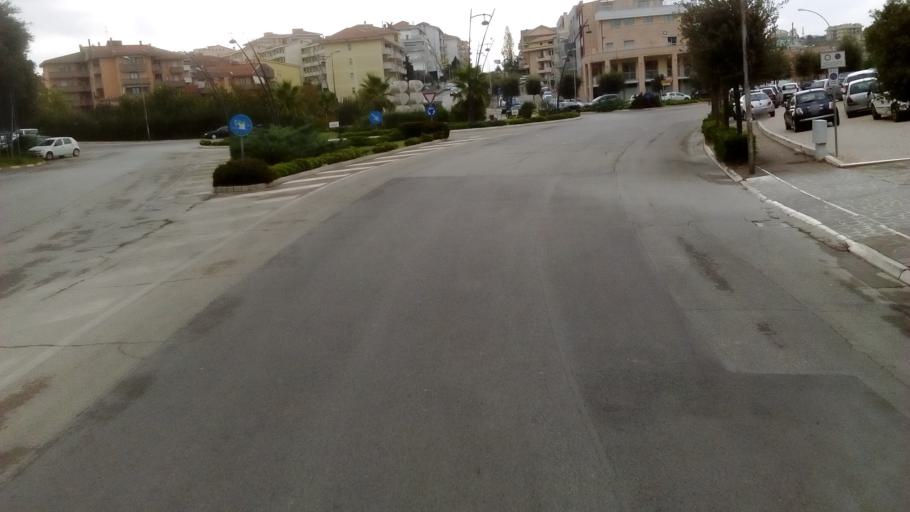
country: IT
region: Abruzzo
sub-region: Provincia di Chieti
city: Vasto
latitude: 42.1082
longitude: 14.7023
